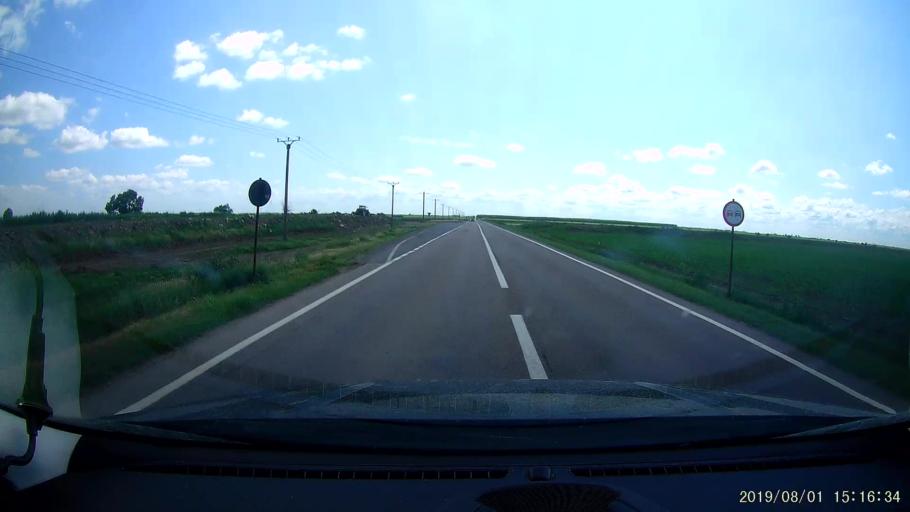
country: RO
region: Braila
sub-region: Comuna Unirea
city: Unirea
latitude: 45.1448
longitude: 27.8508
